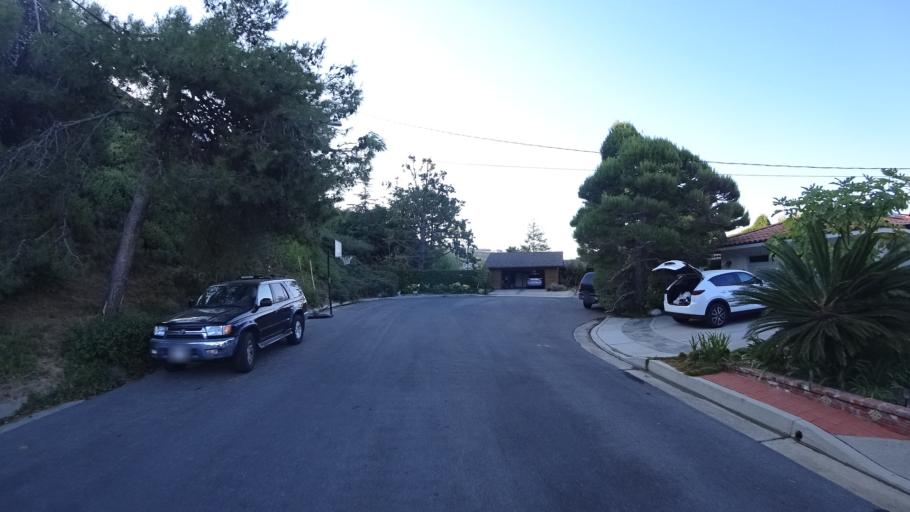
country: US
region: California
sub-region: Orange County
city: San Clemente
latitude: 33.4322
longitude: -117.6027
